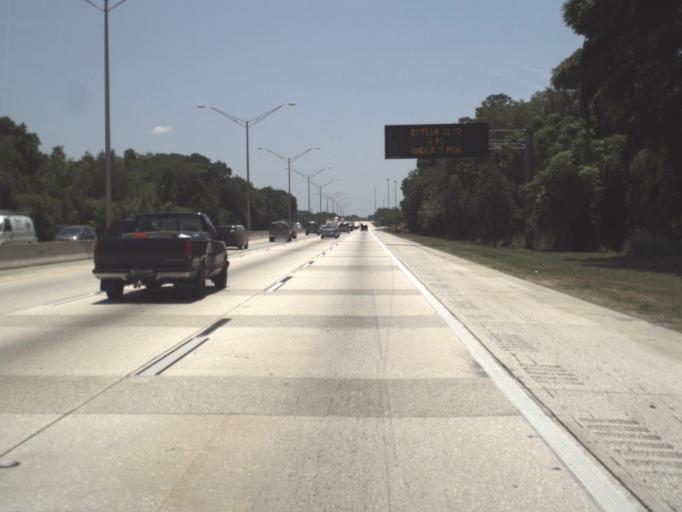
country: US
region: Florida
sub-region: Duval County
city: Jacksonville
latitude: 30.2961
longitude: -81.6358
